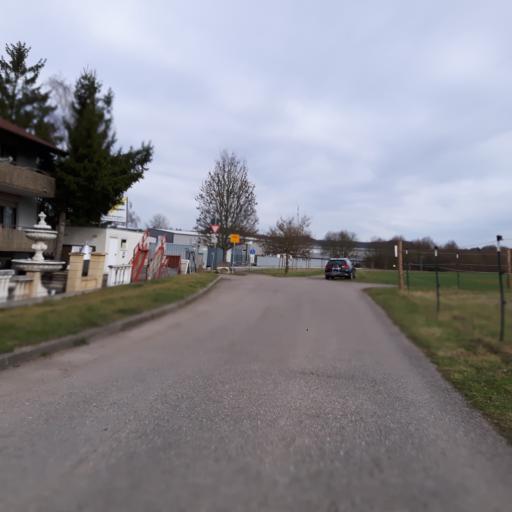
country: DE
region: Baden-Wuerttemberg
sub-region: Regierungsbezirk Stuttgart
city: Abstatt
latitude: 49.0532
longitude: 9.2760
